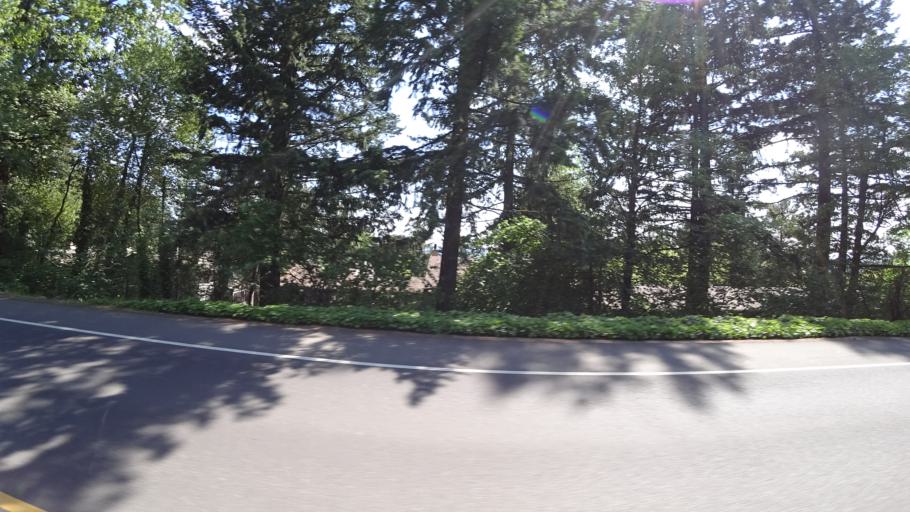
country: US
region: Oregon
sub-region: Washington County
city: Metzger
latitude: 45.4362
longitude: -122.7241
